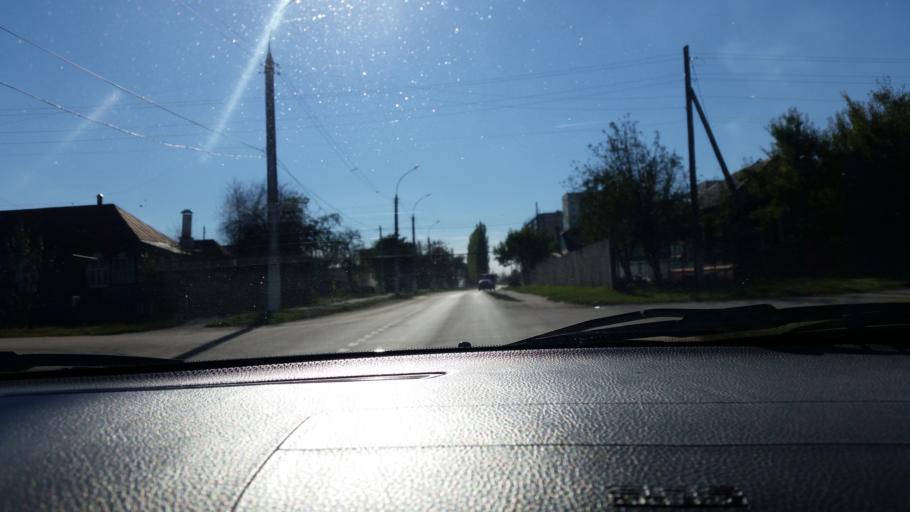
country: RU
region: Lipetsk
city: Gryazi
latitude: 52.4764
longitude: 39.9485
